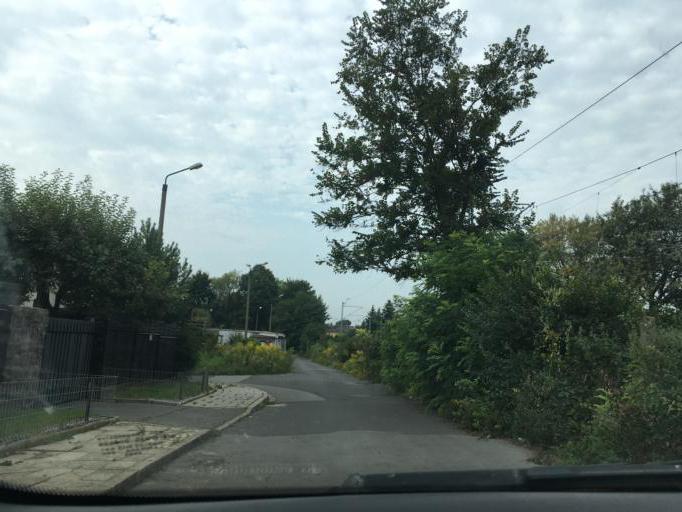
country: PL
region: Lesser Poland Voivodeship
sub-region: Krakow
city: Krakow
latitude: 50.0801
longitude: 19.9469
